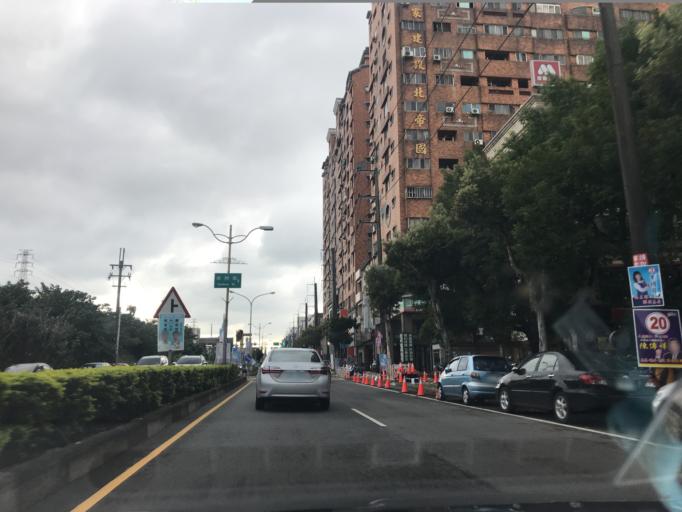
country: TW
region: Taiwan
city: Taoyuan City
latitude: 24.9489
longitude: 121.2364
